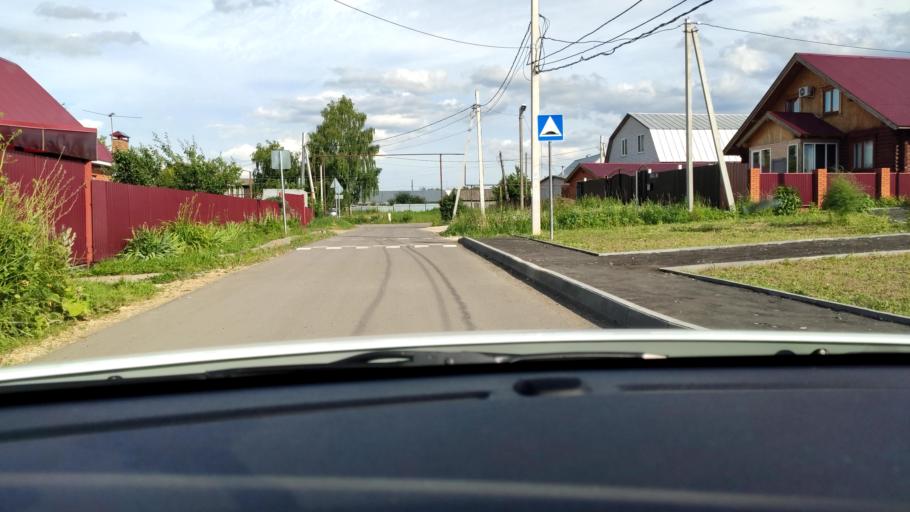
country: RU
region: Tatarstan
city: Stolbishchi
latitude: 55.7406
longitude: 49.2686
